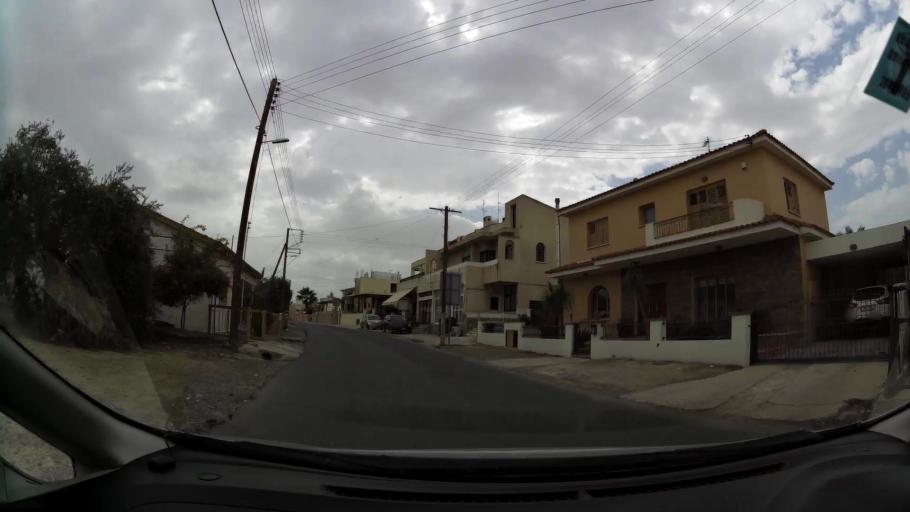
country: CY
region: Lefkosia
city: Geri
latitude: 35.1054
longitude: 33.3746
